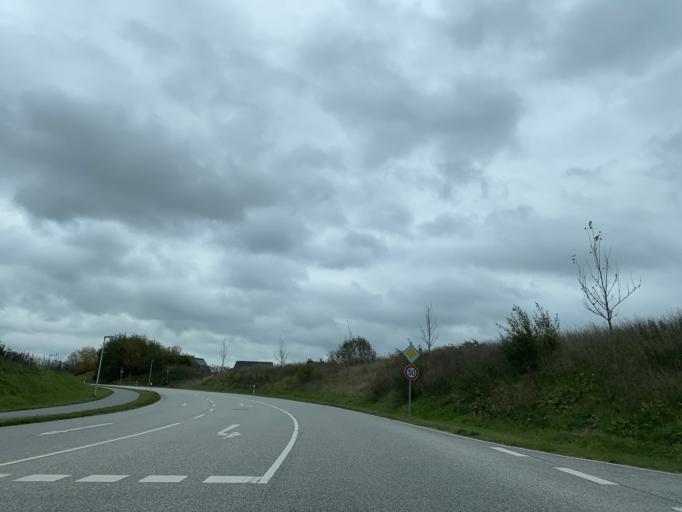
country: DE
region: Schleswig-Holstein
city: Tastrup
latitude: 54.7704
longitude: 9.4662
